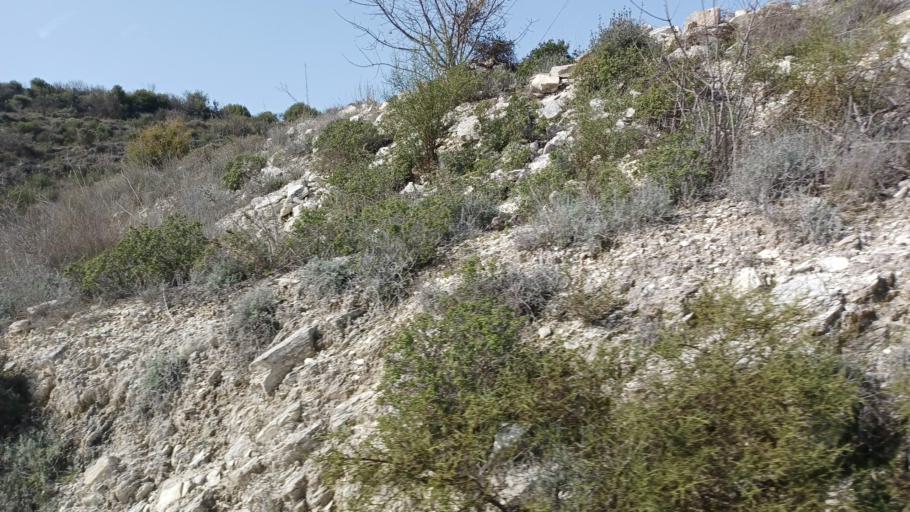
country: CY
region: Limassol
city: Pachna
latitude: 34.8015
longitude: 32.6933
